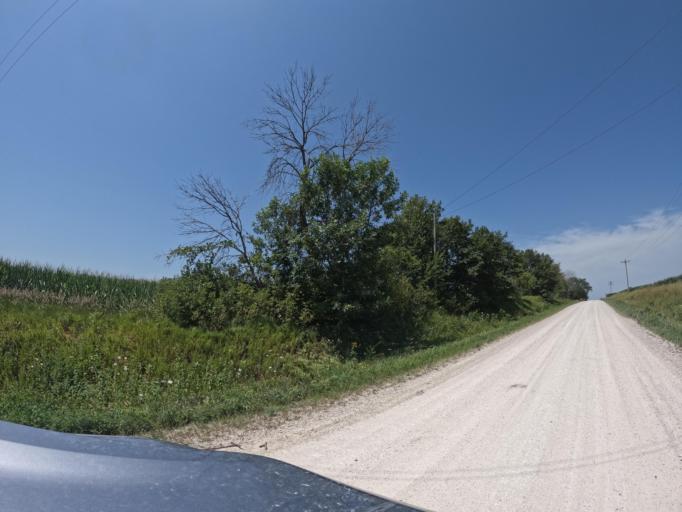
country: US
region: Iowa
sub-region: Henry County
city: Mount Pleasant
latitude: 40.9452
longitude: -91.6606
